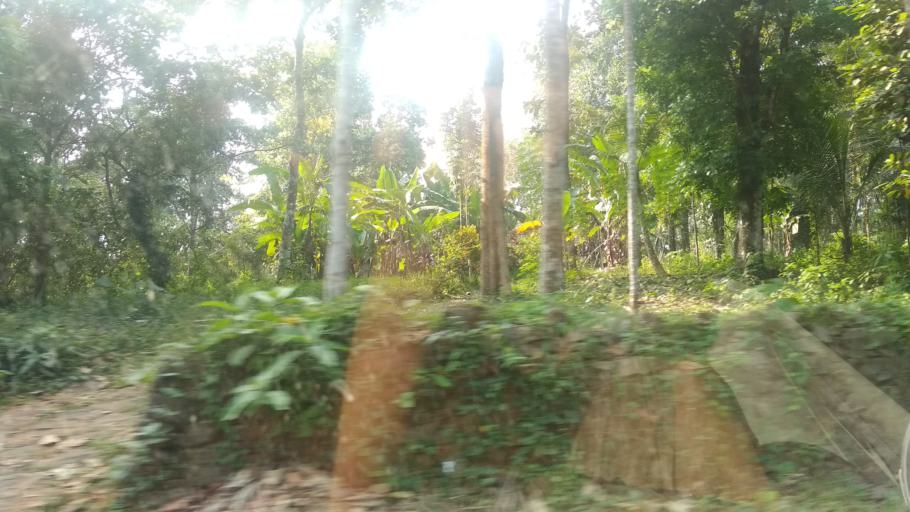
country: IN
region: Kerala
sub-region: Kottayam
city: Changanacheri
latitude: 9.5068
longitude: 76.6866
